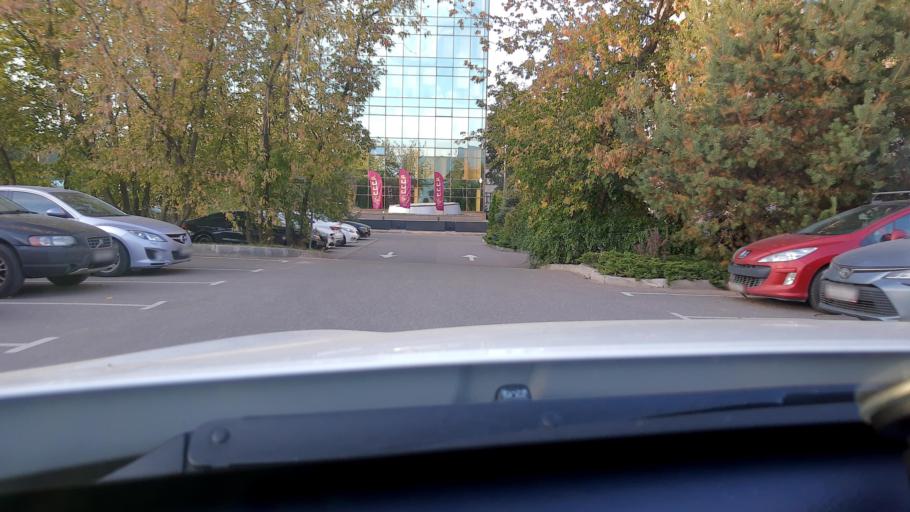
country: RU
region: Moscow
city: Ochakovo-Matveyevskoye
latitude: 55.7085
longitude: 37.4430
